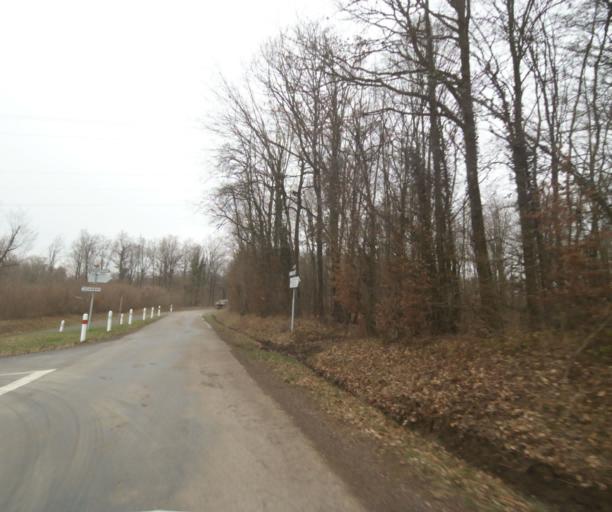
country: FR
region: Champagne-Ardenne
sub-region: Departement de la Haute-Marne
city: Wassy
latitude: 48.5181
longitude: 4.9705
